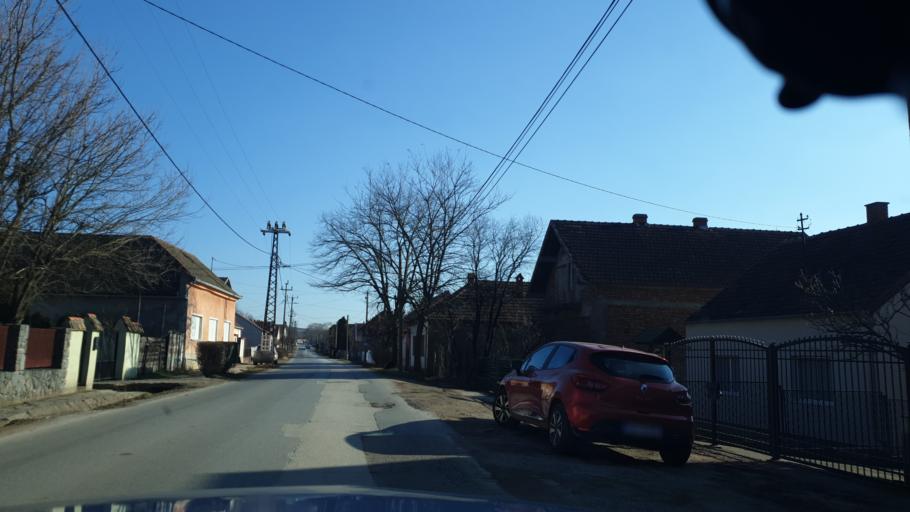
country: RS
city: Vrdnik
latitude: 45.1263
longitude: 19.7896
